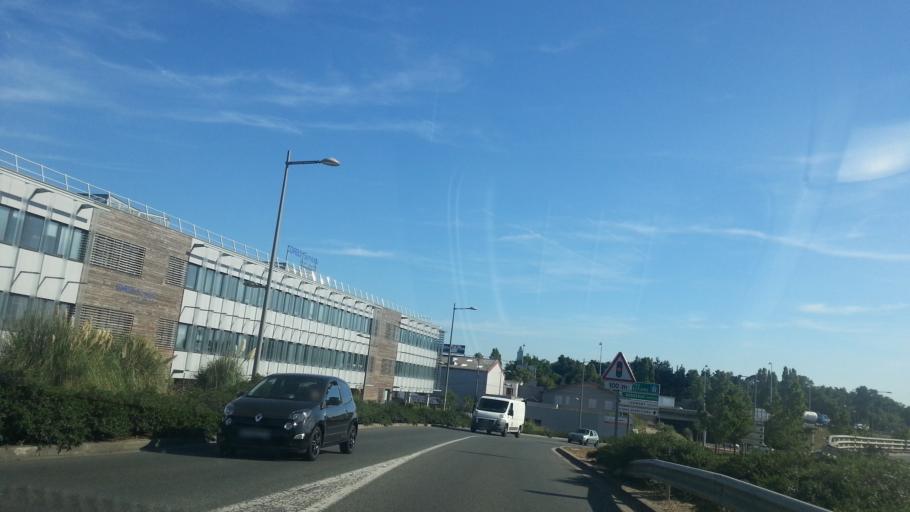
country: FR
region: Aquitaine
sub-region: Departement de la Gironde
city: Lormont
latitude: 44.8864
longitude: -0.5174
